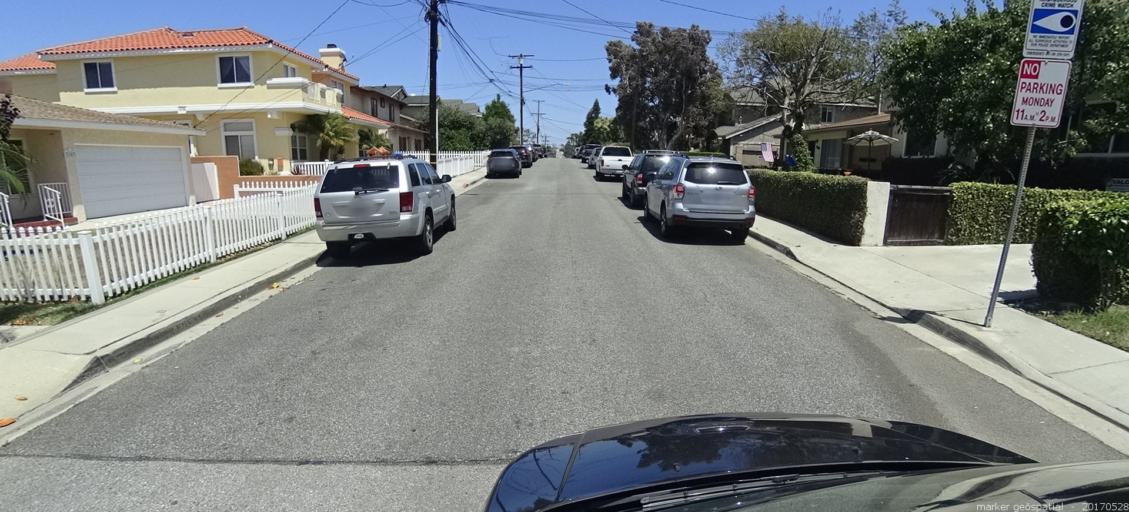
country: US
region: California
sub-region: Los Angeles County
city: Redondo Beach
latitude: 33.8643
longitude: -118.3747
